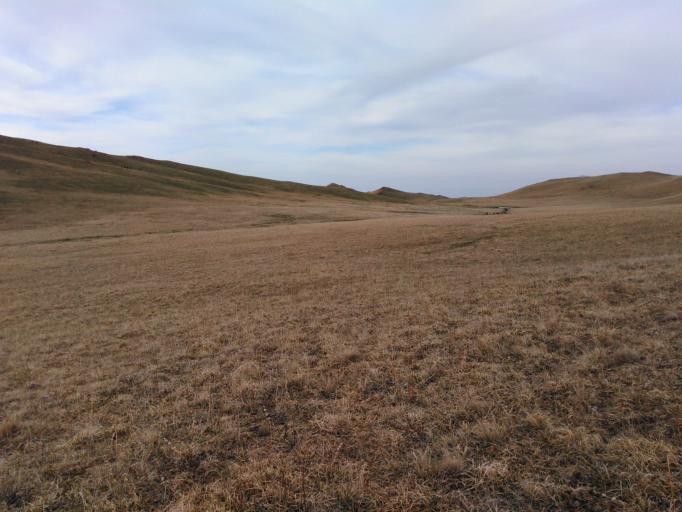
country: KG
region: Naryn
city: Kochkor
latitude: 42.4976
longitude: 75.7374
